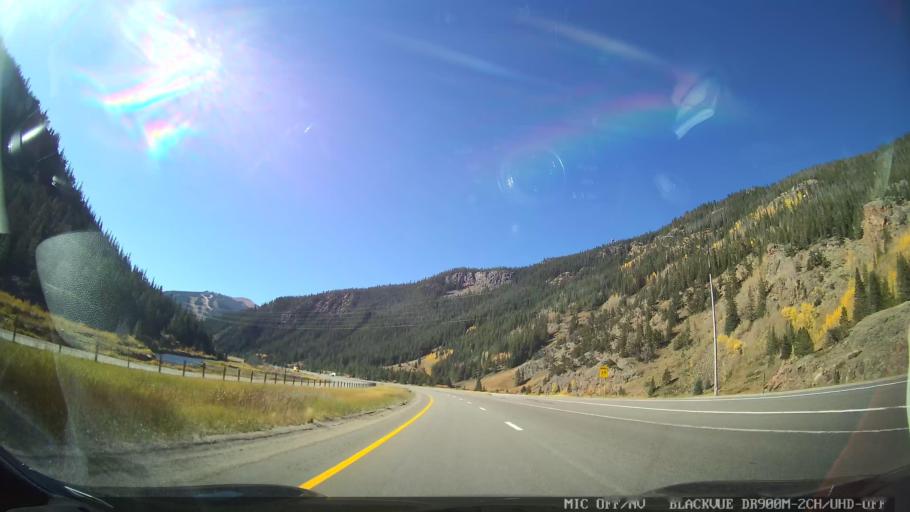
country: US
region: Colorado
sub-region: Summit County
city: Frisco
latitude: 39.5223
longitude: -106.1441
